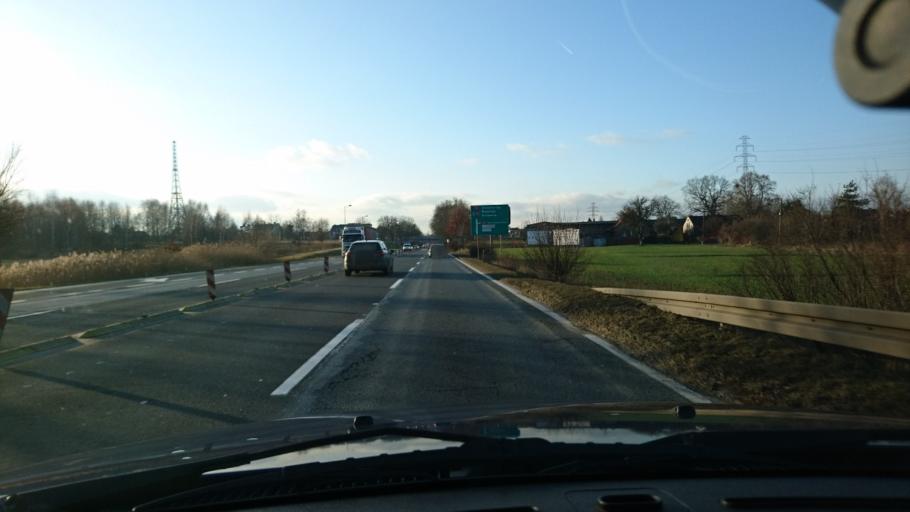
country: PL
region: Silesian Voivodeship
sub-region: Gliwice
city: Gliwice
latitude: 50.3142
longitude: 18.6984
